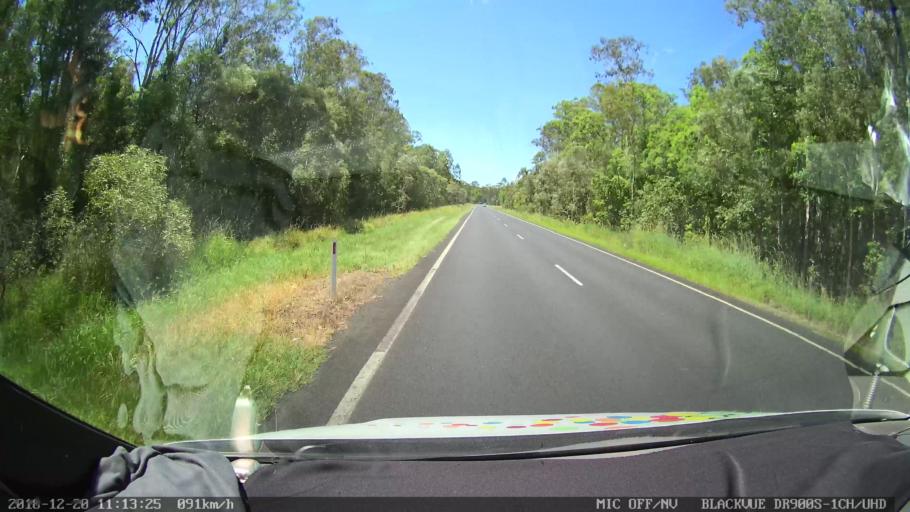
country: AU
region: New South Wales
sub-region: Richmond Valley
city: Casino
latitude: -28.9872
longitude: 153.0106
